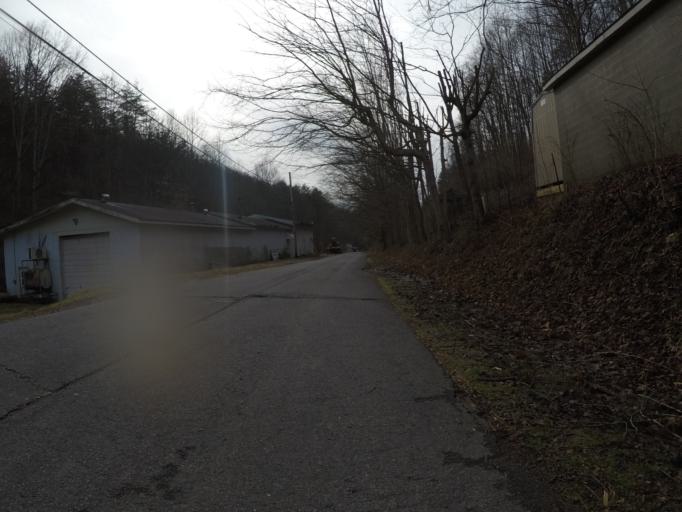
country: US
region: West Virginia
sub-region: Wayne County
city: Lavalette
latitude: 38.3364
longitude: -82.3769
